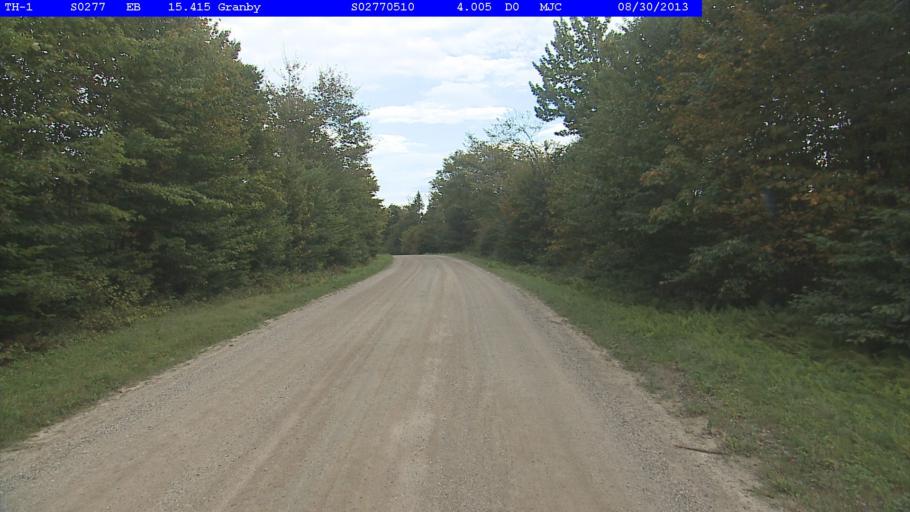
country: US
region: Vermont
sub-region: Essex County
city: Guildhall
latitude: 44.5756
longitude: -71.6925
